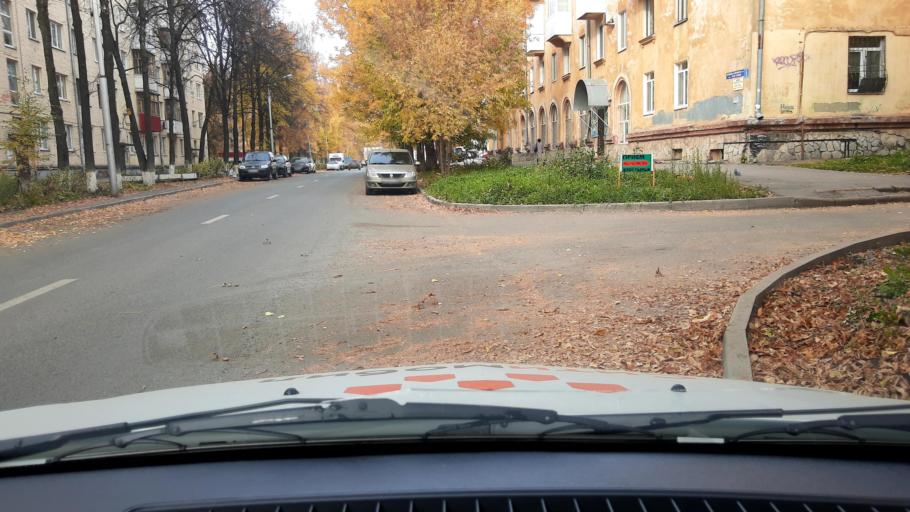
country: RU
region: Bashkortostan
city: Ufa
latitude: 54.8136
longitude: 56.0954
